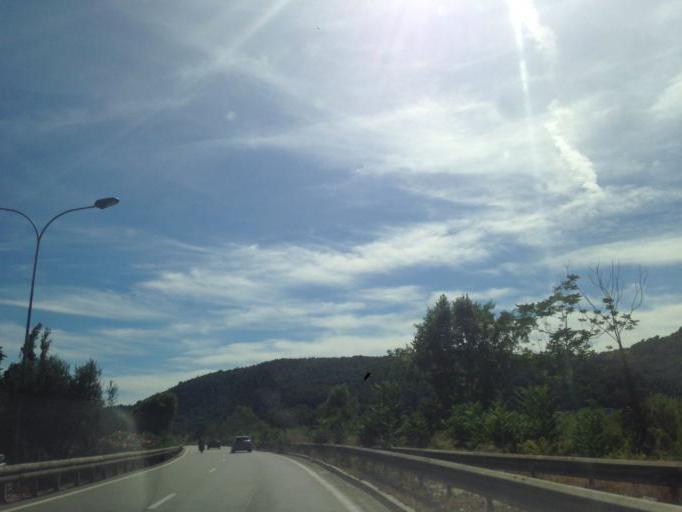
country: FR
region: Provence-Alpes-Cote d'Azur
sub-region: Departement des Alpes-Maritimes
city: Gattieres
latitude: 43.7472
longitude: 7.1881
